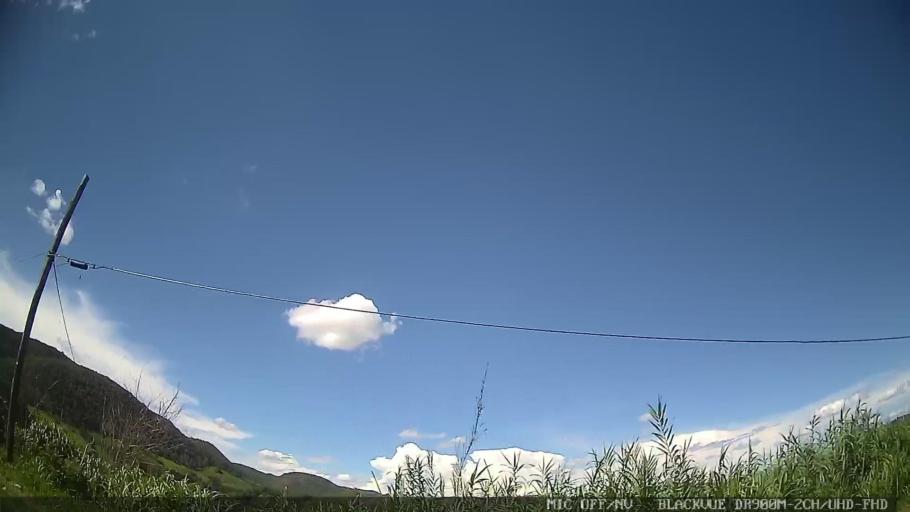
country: BR
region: Sao Paulo
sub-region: Amparo
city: Amparo
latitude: -22.7106
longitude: -46.8319
